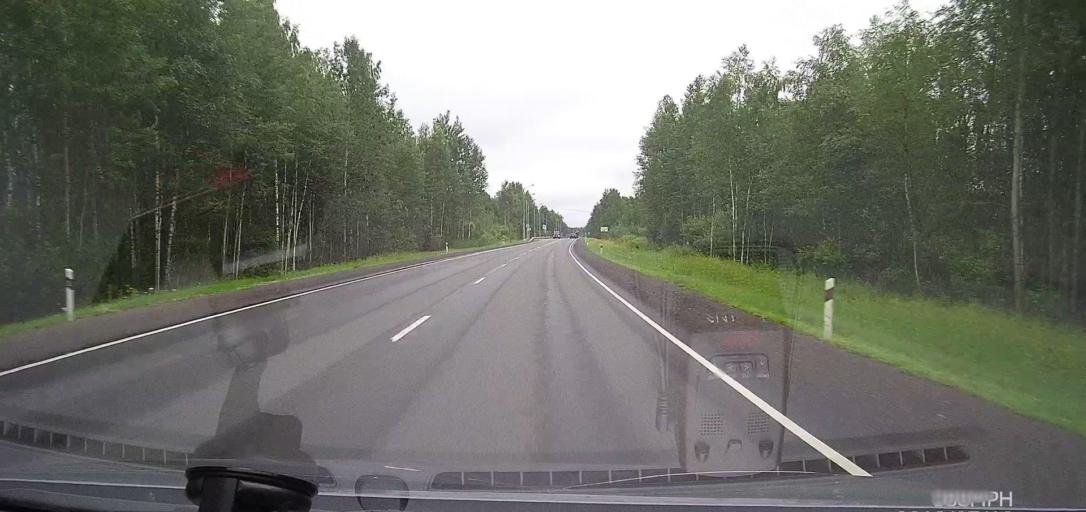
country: RU
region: Leningrad
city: Syas'stroy
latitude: 60.1955
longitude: 32.6590
